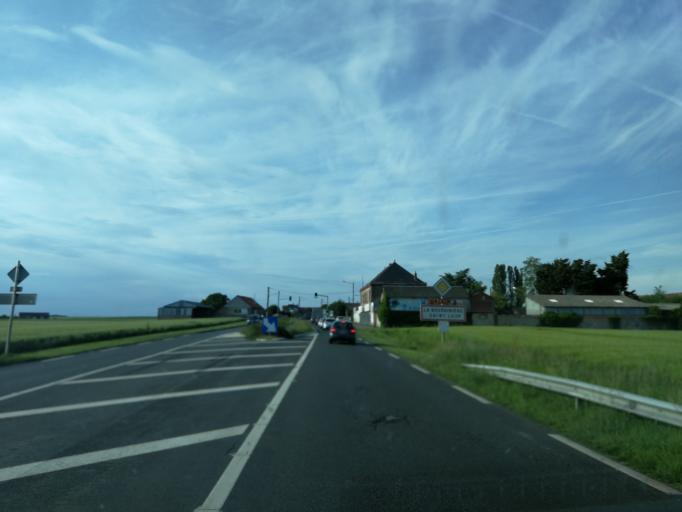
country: FR
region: Centre
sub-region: Departement d'Eure-et-Loir
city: Dammarie
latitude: 48.3132
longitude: 1.4262
